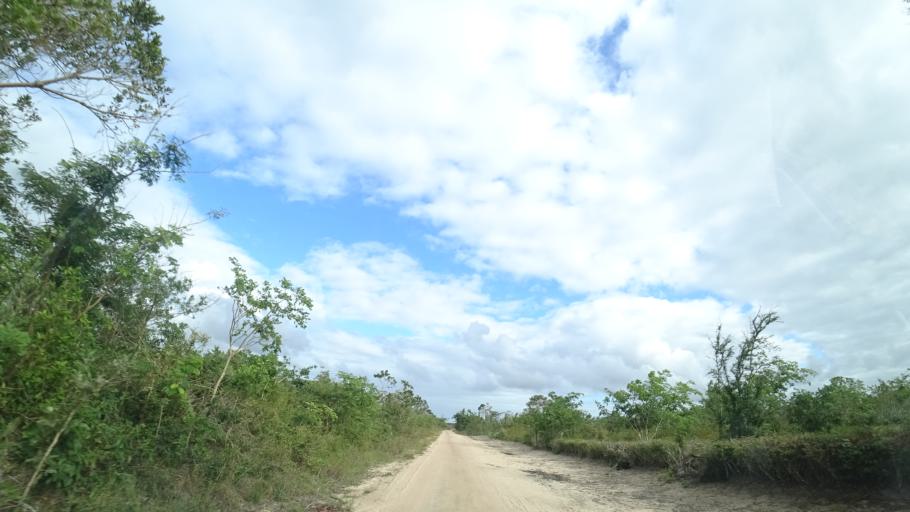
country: MZ
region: Sofala
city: Beira
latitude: -19.6415
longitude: 35.0592
